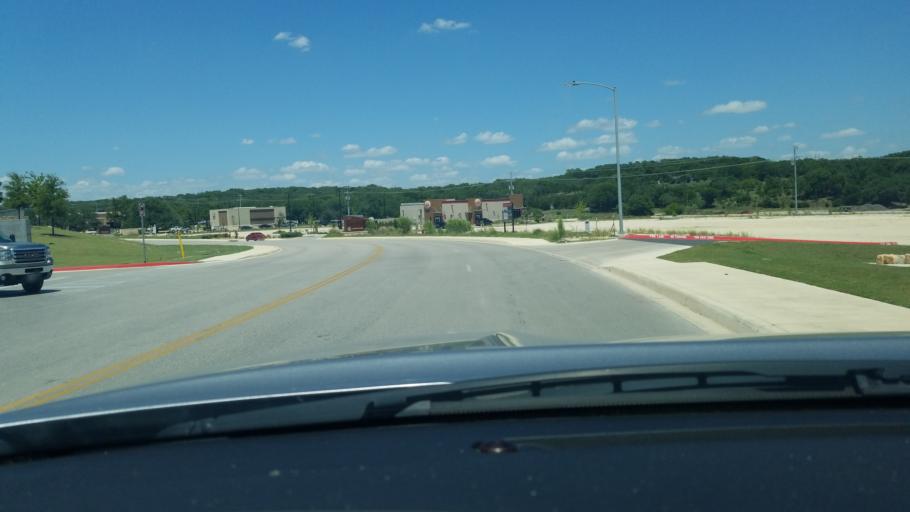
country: US
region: Texas
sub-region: Comal County
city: Bulverde
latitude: 29.7999
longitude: -98.4210
